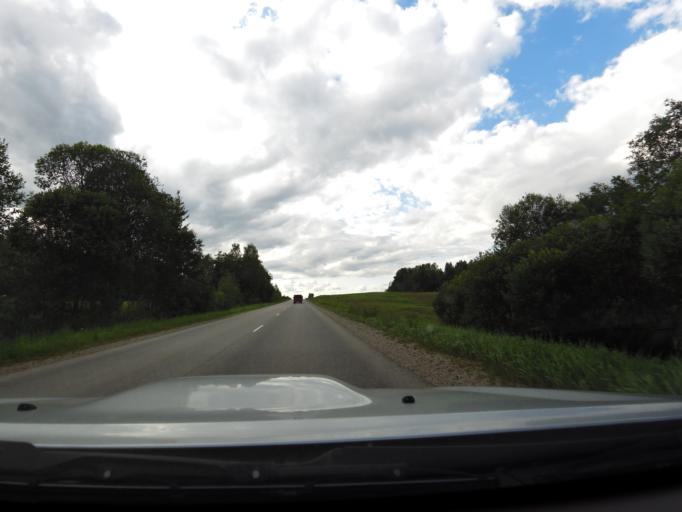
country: LV
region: Ilukste
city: Ilukste
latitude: 55.9700
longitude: 26.0313
